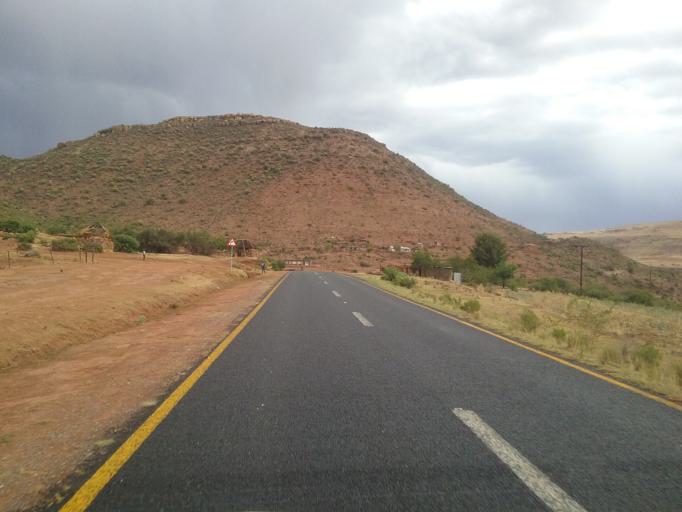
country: LS
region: Quthing
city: Quthing
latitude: -30.3553
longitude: 27.7266
